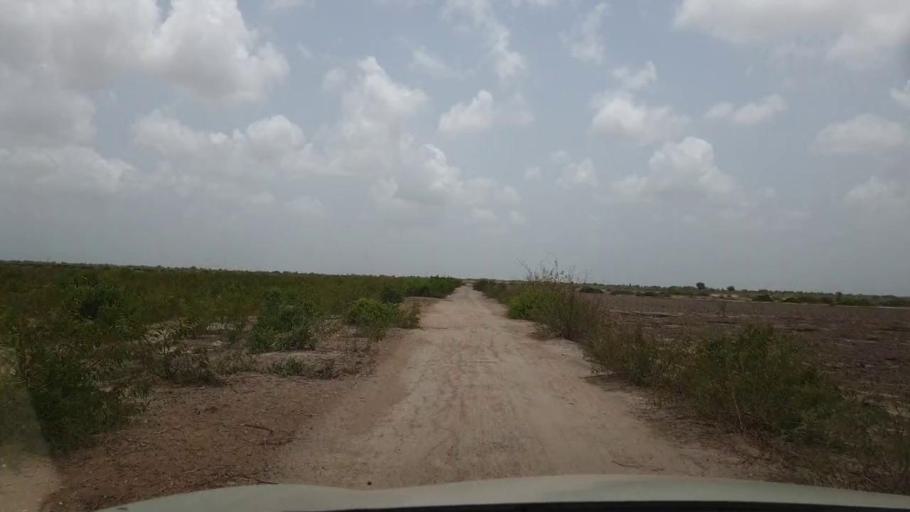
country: PK
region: Sindh
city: Chambar
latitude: 25.2297
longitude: 68.7596
